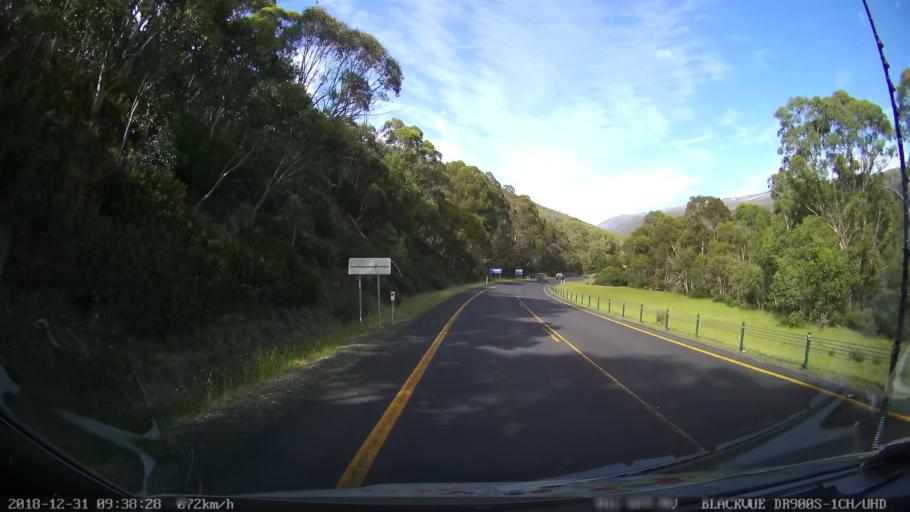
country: AU
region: New South Wales
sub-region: Snowy River
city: Jindabyne
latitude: -36.4744
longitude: 148.3673
